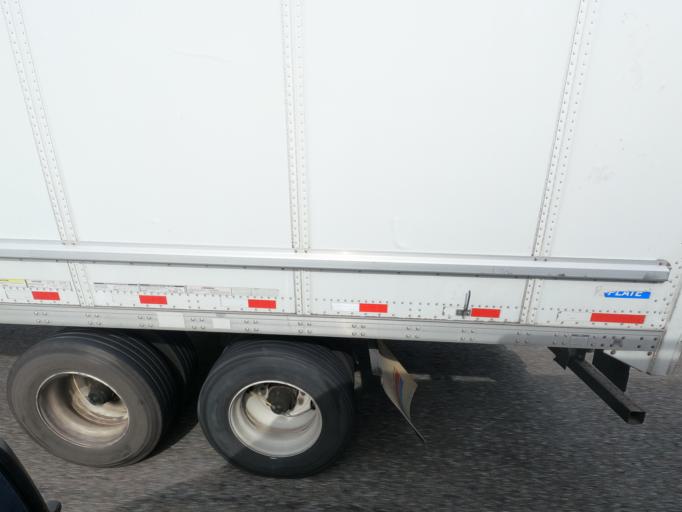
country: US
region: Tennessee
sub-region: Henderson County
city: Lexington
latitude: 35.7993
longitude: -88.3568
